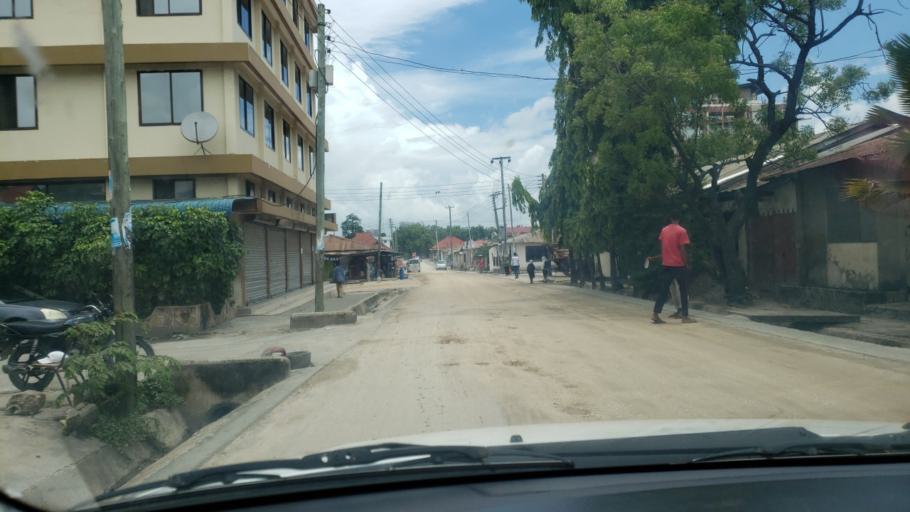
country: TZ
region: Dar es Salaam
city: Magomeni
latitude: -6.8115
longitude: 39.2587
